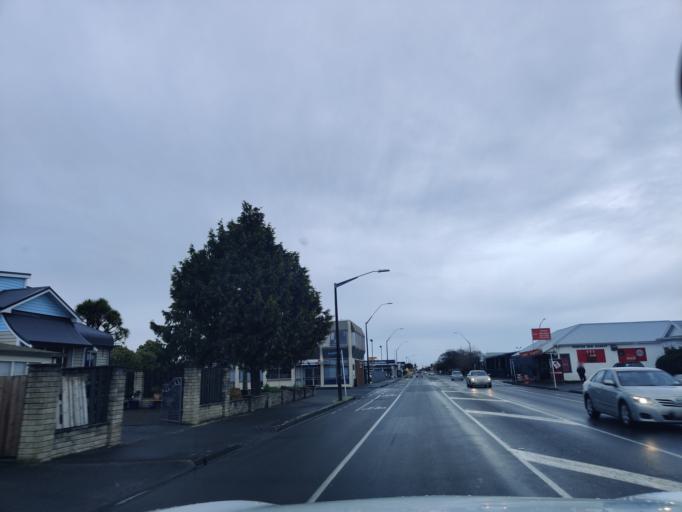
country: NZ
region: Manawatu-Wanganui
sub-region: Palmerston North City
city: Palmerston North
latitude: -40.3476
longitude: 175.6115
